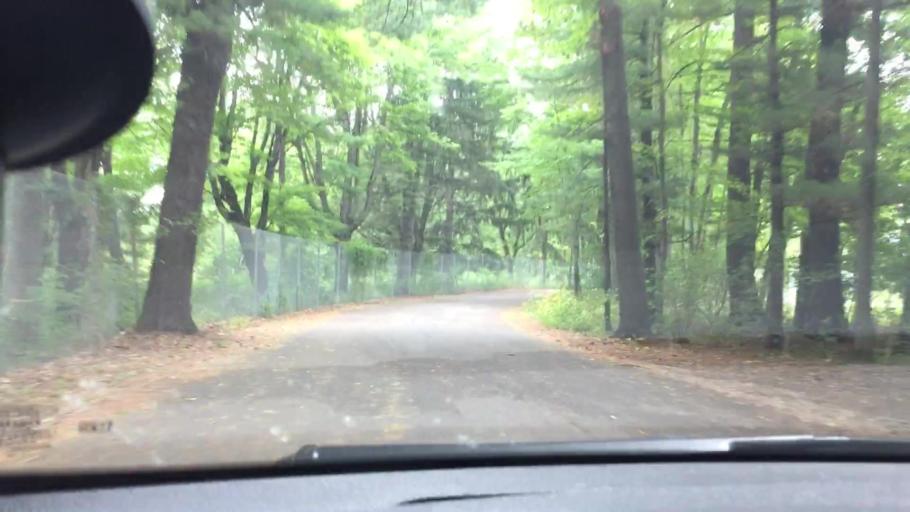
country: US
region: Wisconsin
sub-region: Chippewa County
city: Chippewa Falls
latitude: 44.9531
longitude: -91.4023
